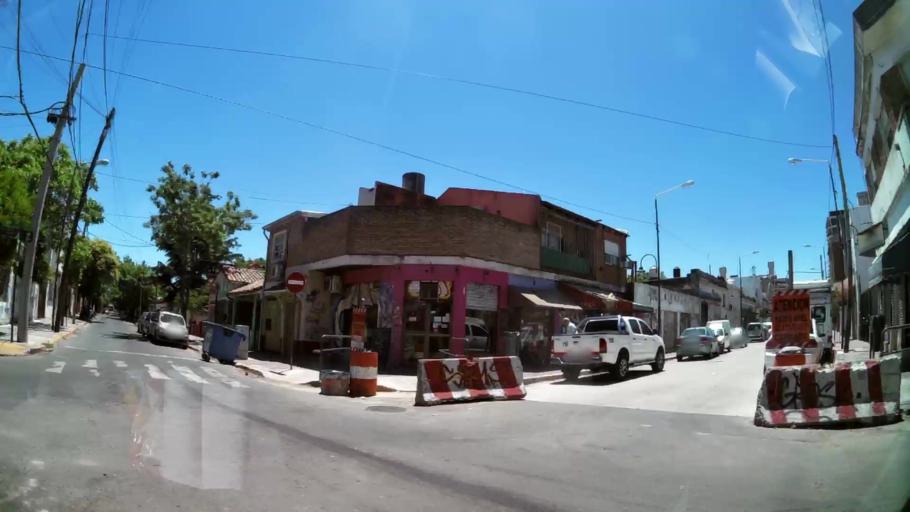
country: AR
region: Buenos Aires
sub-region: Partido de Tigre
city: Tigre
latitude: -34.4457
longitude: -58.5588
